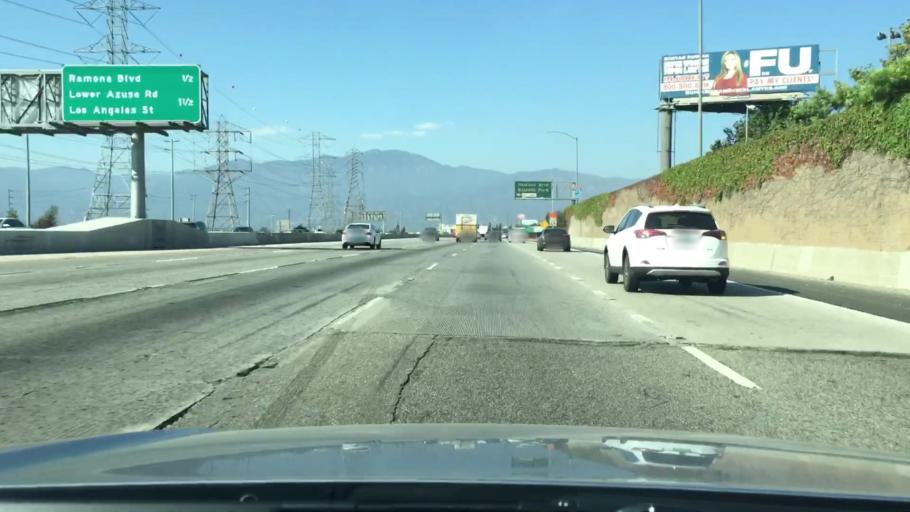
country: US
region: California
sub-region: Los Angeles County
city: El Monte
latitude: 34.0705
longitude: -118.0001
